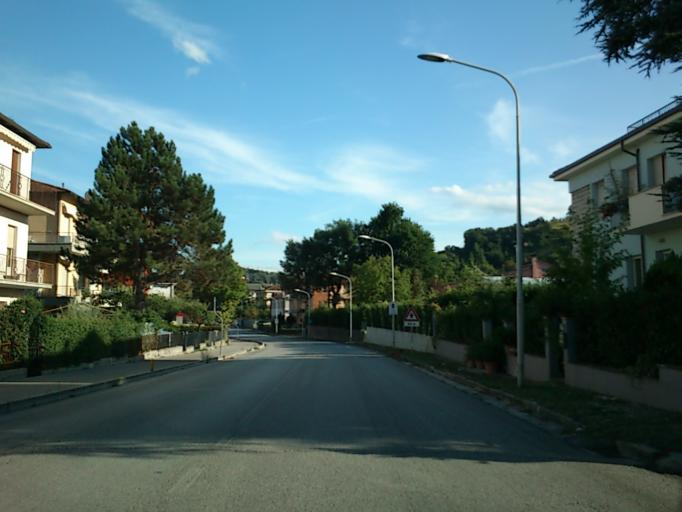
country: IT
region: The Marches
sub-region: Provincia di Pesaro e Urbino
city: Urbania
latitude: 43.6678
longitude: 12.5172
